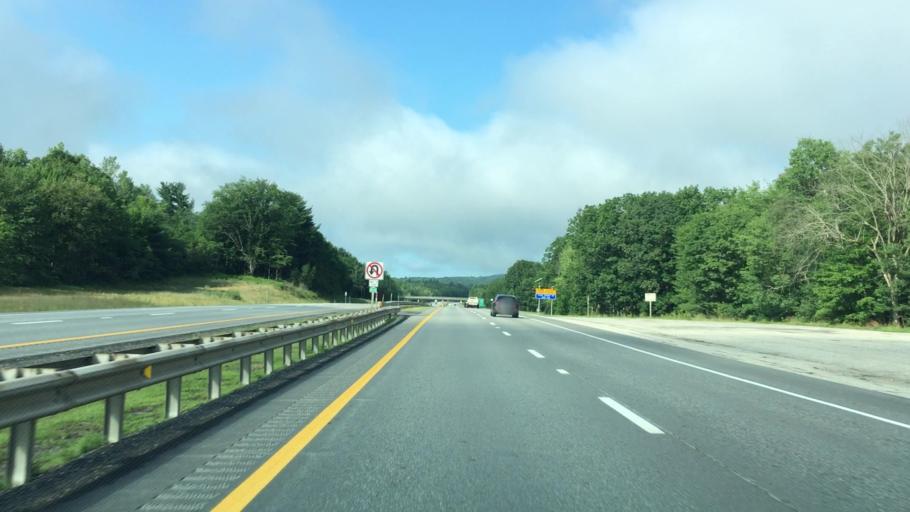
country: US
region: Maine
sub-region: Androscoggin County
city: Lisbon
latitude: 44.0735
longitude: -70.1319
